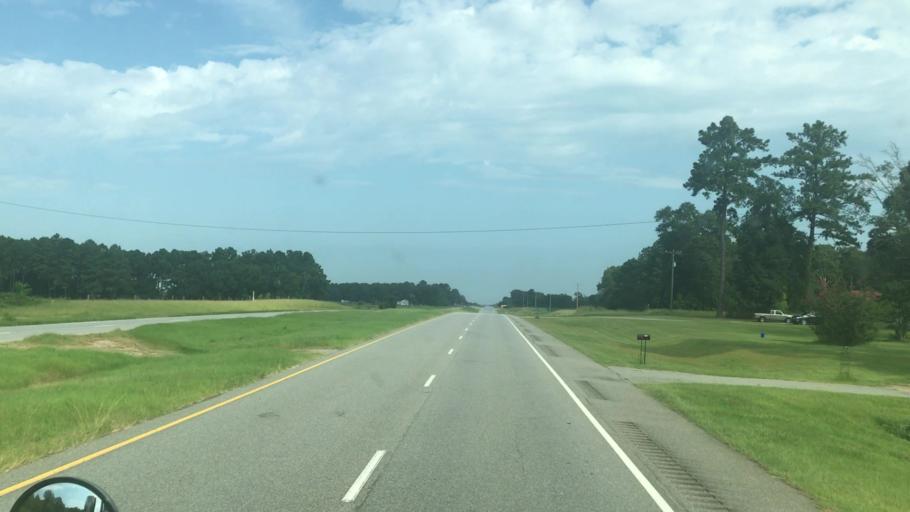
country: US
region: Georgia
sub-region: Early County
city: Blakely
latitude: 31.3122
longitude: -84.8730
